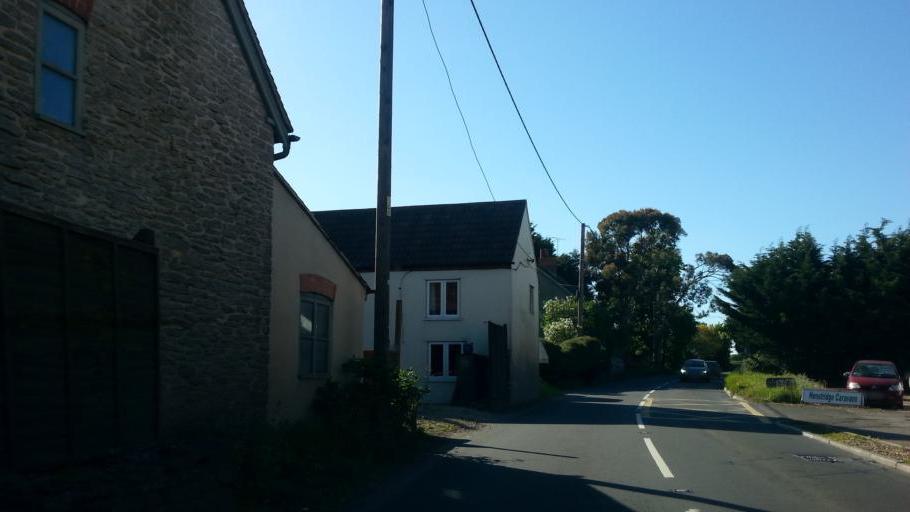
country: GB
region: England
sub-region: Dorset
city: Stalbridge
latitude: 50.9803
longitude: -2.3993
